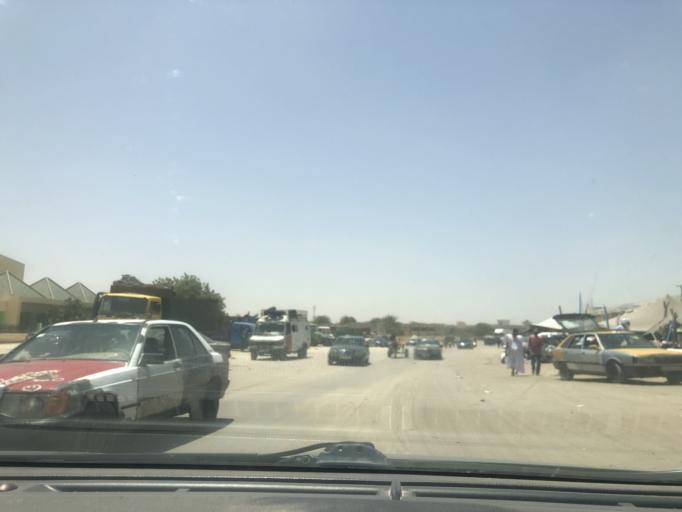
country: MR
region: Nouakchott
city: Nouakchott
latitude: 18.0773
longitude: -15.9823
